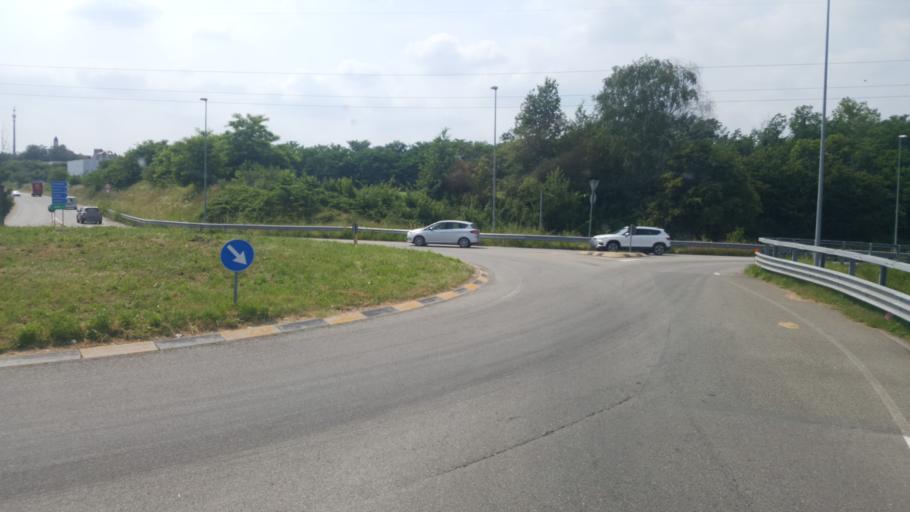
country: IT
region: Lombardy
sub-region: Provincia di Como
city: Luisago
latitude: 45.7699
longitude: 9.0381
